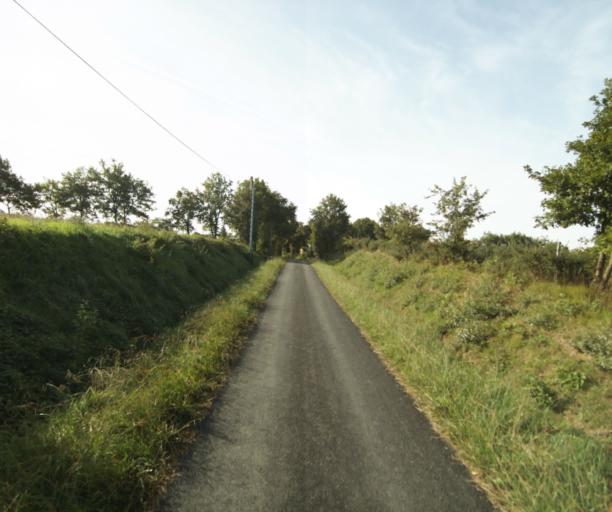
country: FR
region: Midi-Pyrenees
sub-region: Departement du Gers
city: Eauze
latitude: 43.8933
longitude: 0.1327
